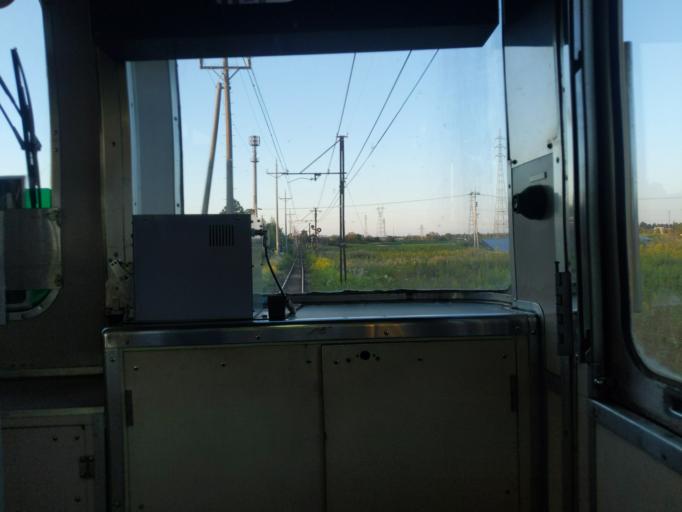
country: JP
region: Toyama
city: Kamiichi
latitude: 36.6932
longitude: 137.3183
